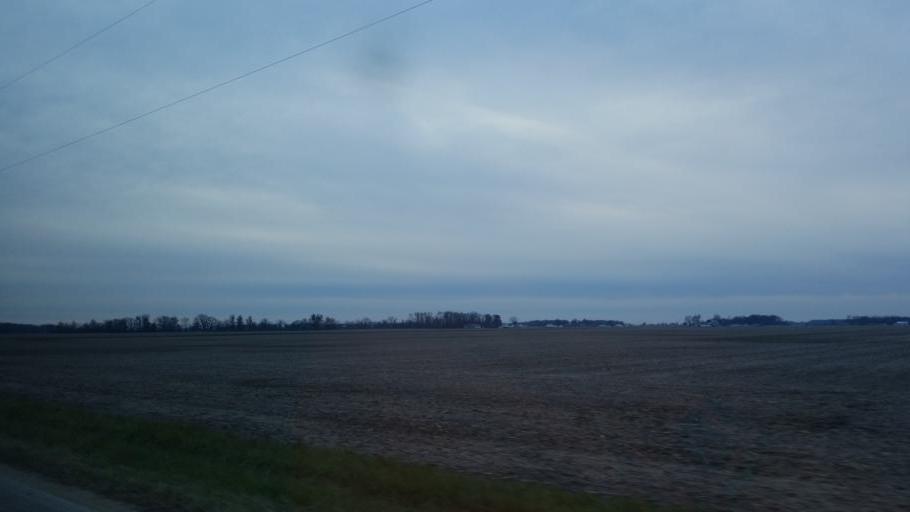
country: US
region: Indiana
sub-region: Adams County
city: Decatur
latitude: 40.7783
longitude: -84.8799
